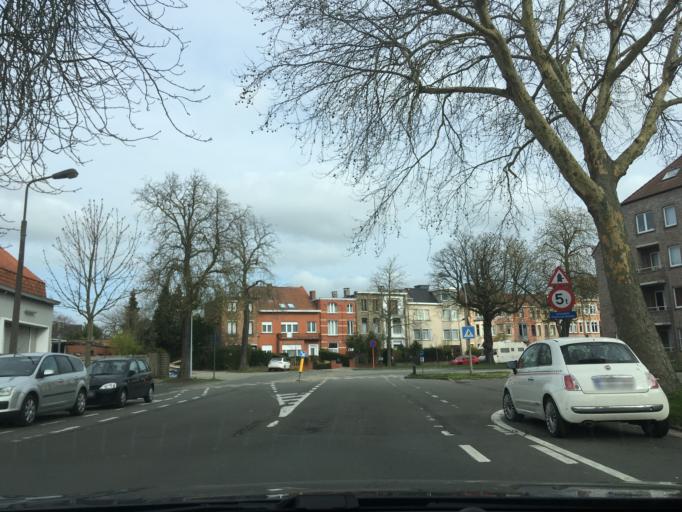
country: BE
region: Flanders
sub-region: Provincie West-Vlaanderen
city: Kortrijk
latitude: 50.8328
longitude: 3.2546
